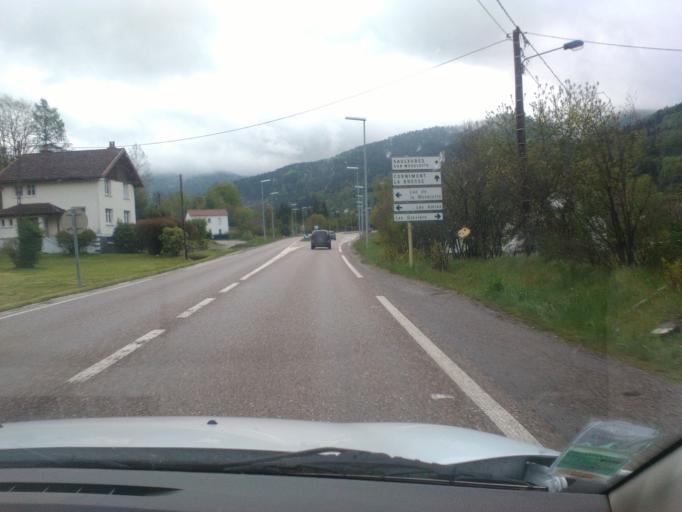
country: FR
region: Lorraine
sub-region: Departement des Vosges
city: Saulxures-sur-Moselotte
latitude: 47.9579
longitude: 6.7427
